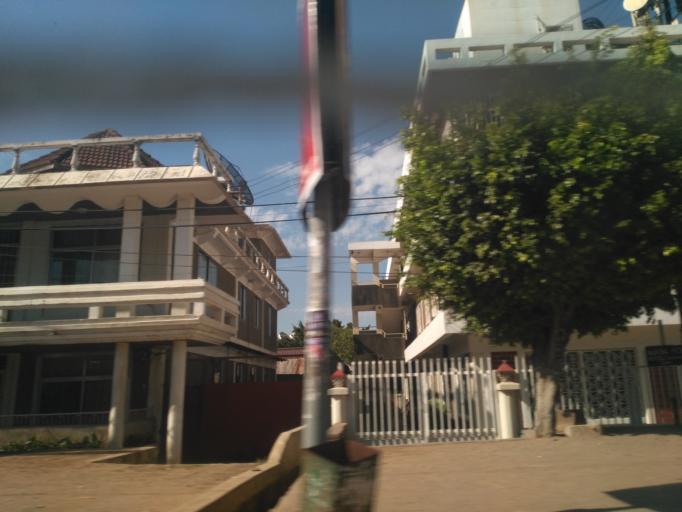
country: TZ
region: Mwanza
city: Mwanza
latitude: -2.5038
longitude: 32.8979
